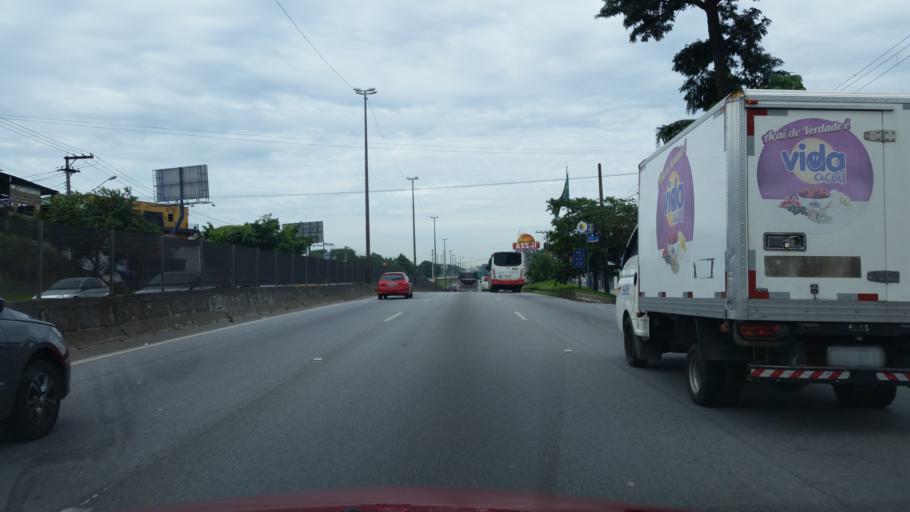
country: BR
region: Sao Paulo
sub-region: Taboao Da Serra
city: Taboao da Serra
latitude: -23.6127
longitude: -46.7793
